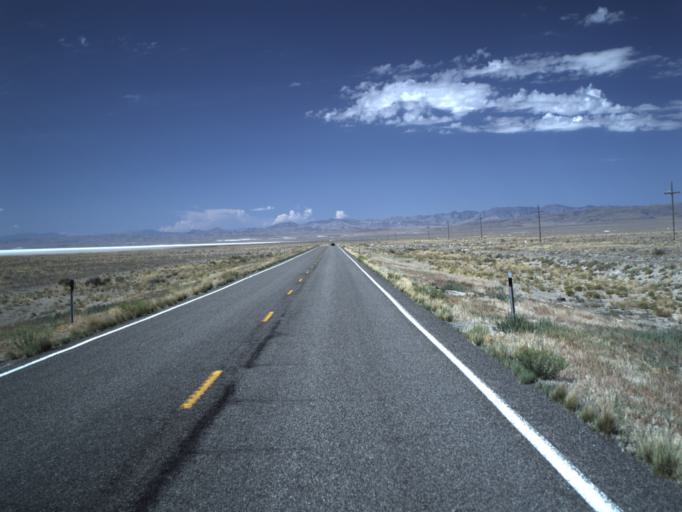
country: US
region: Utah
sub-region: Millard County
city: Delta
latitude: 39.1334
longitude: -113.0981
